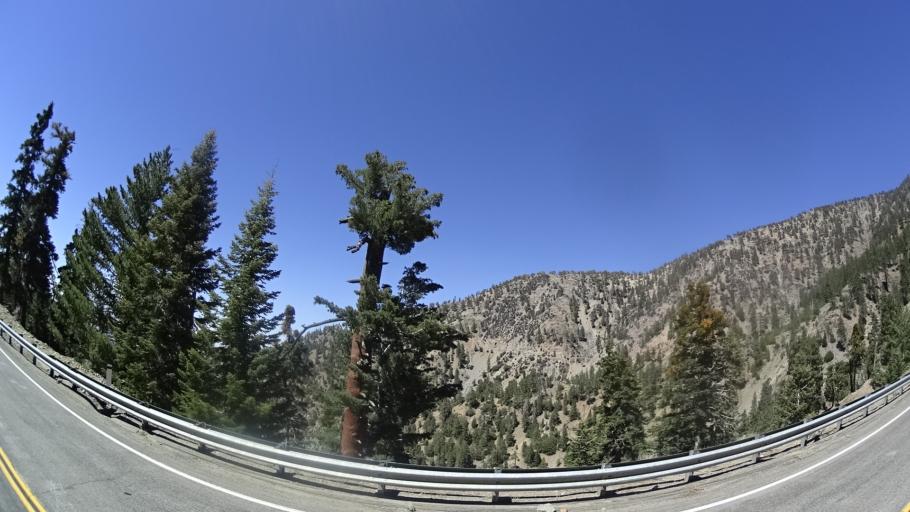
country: US
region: California
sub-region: San Bernardino County
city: Wrightwood
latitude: 34.3487
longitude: -117.8146
